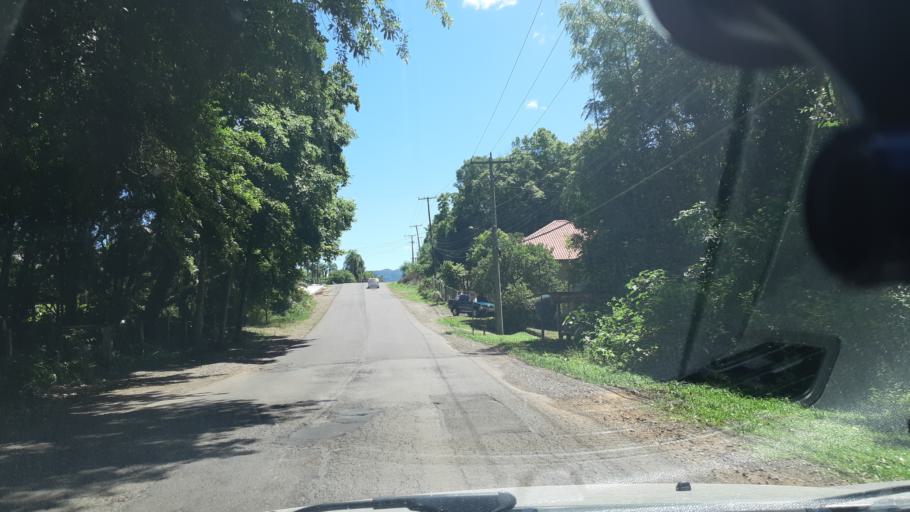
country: BR
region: Rio Grande do Sul
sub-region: Ivoti
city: Ivoti
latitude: -29.6142
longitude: -51.0921
